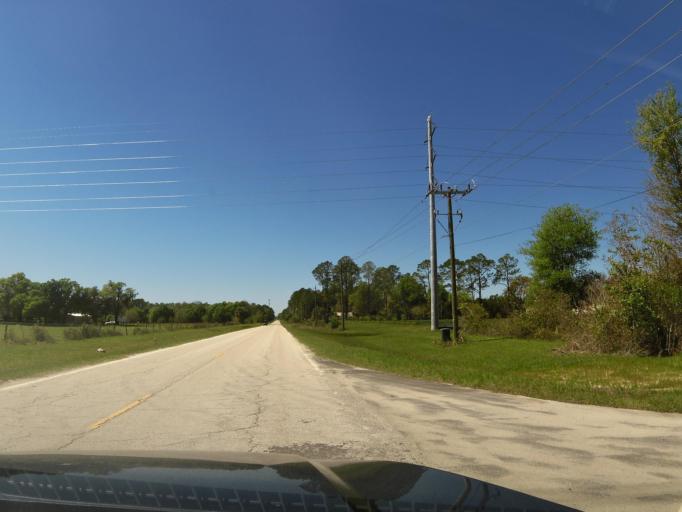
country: US
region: Florida
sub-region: Bradford County
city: Starke
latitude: 30.0559
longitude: -82.0557
